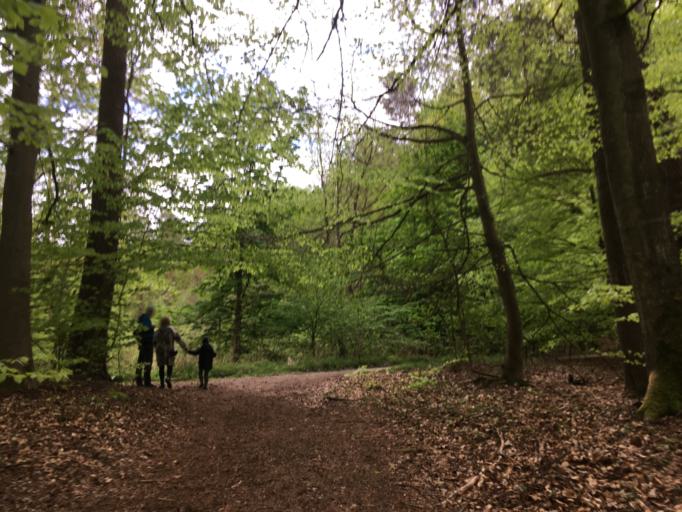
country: DE
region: Brandenburg
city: Rudnitz
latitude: 52.7379
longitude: 13.5985
